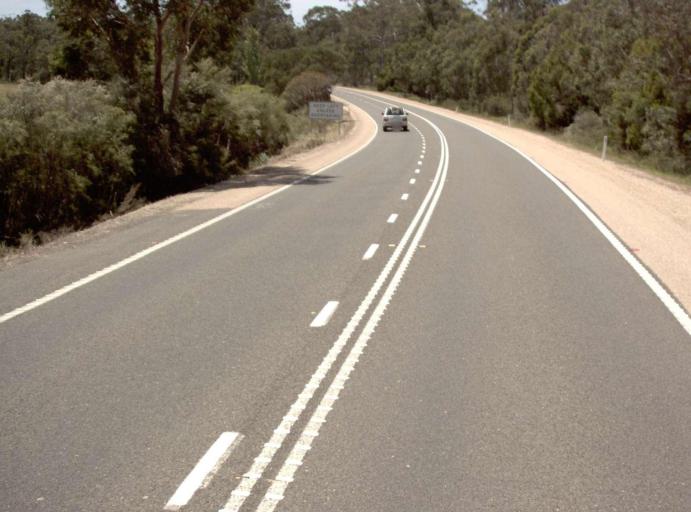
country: AU
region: Victoria
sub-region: East Gippsland
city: Bairnsdale
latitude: -37.7456
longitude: 147.7599
